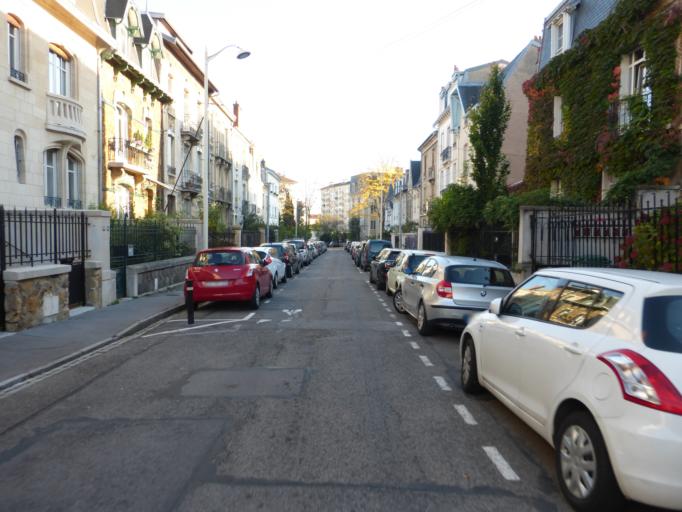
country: FR
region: Lorraine
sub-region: Departement de Meurthe-et-Moselle
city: Nancy
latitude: 48.6769
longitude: 6.1823
